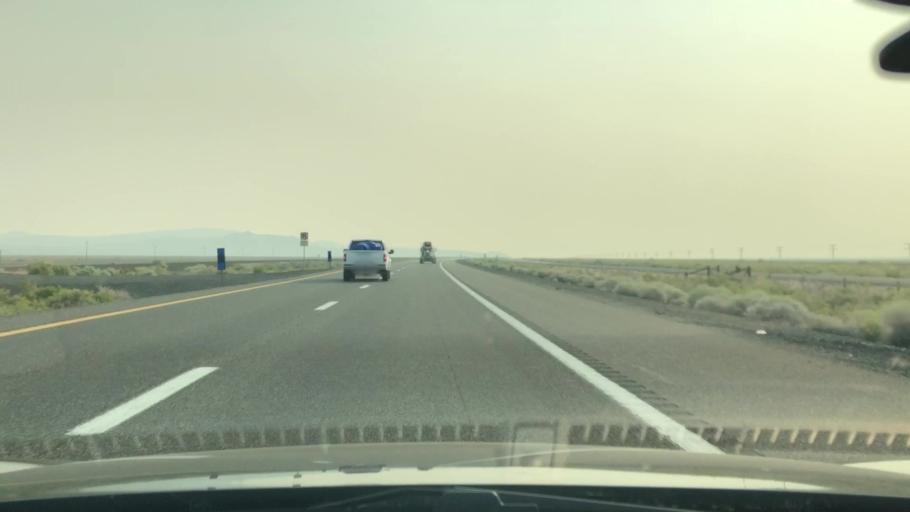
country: US
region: Nevada
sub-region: Pershing County
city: Lovelock
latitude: 40.0751
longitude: -118.6313
